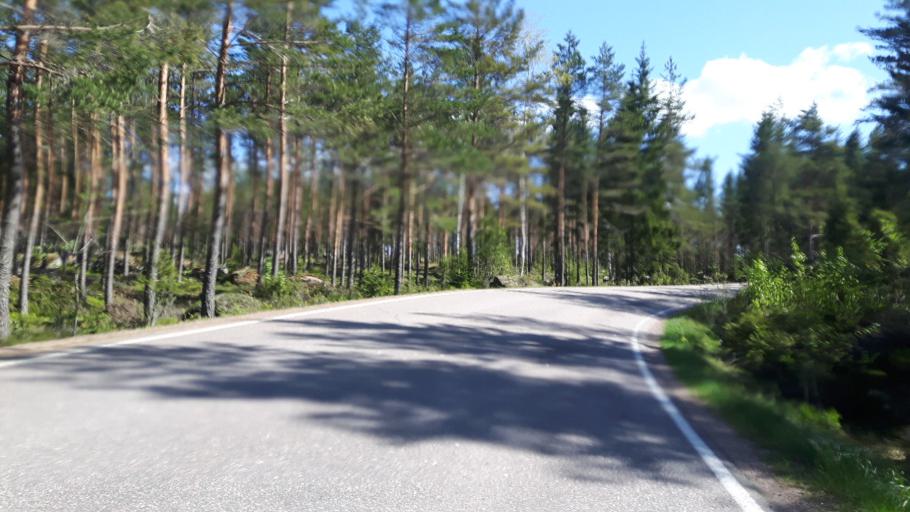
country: FI
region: Kymenlaakso
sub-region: Kotka-Hamina
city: Hamina
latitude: 60.5135
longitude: 27.3887
